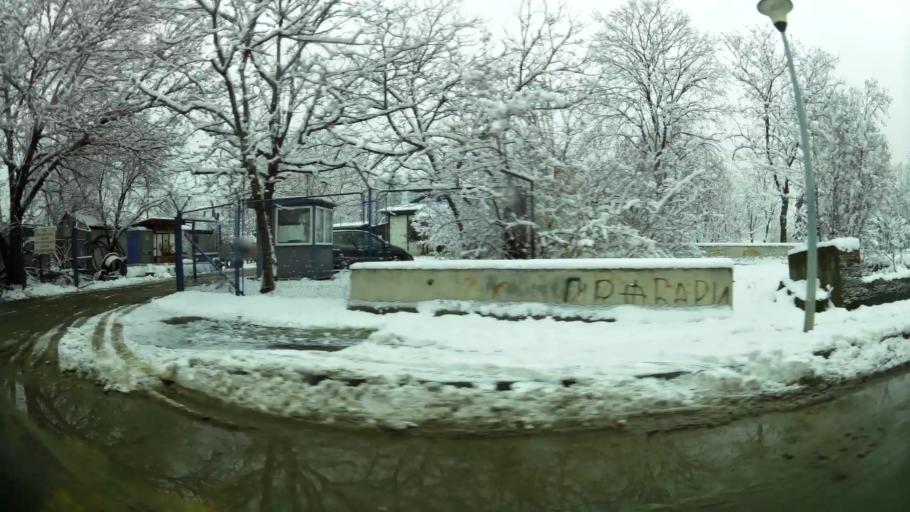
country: RS
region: Central Serbia
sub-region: Belgrade
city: Novi Beograd
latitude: 44.8093
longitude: 20.4434
